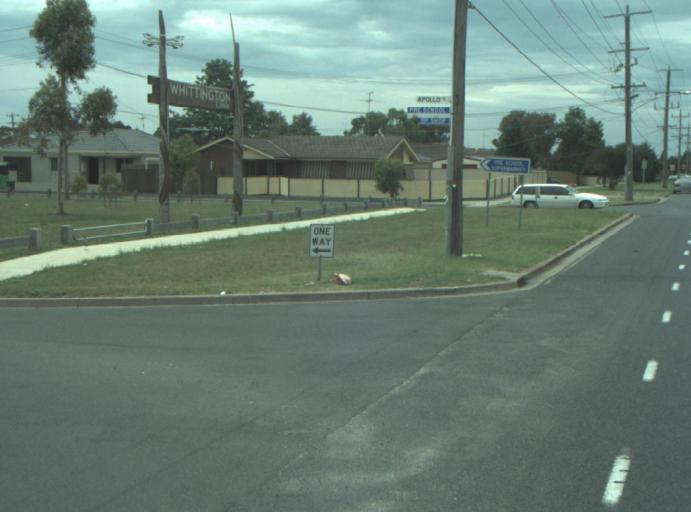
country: AU
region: Victoria
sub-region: Greater Geelong
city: Breakwater
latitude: -38.1816
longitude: 144.3942
